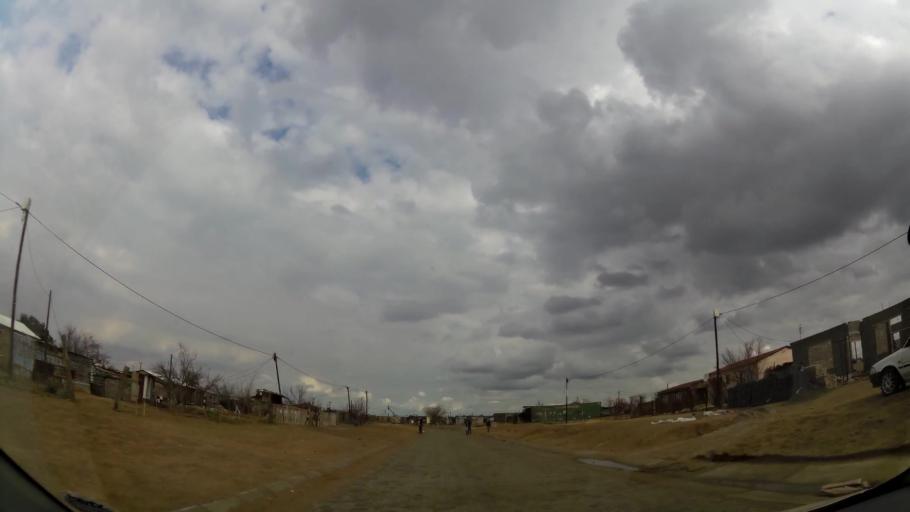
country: ZA
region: Orange Free State
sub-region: Fezile Dabi District Municipality
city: Sasolburg
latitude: -26.8830
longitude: 27.8825
